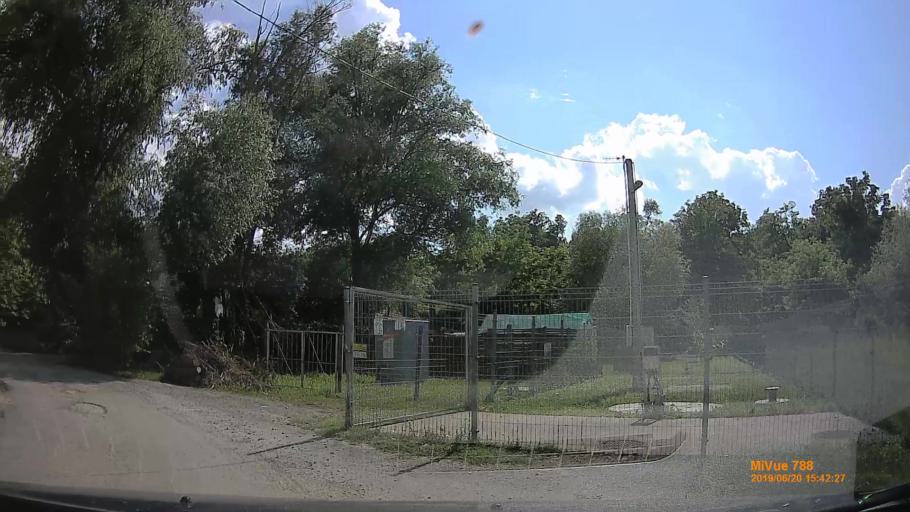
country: HU
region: Baranya
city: Kozarmisleny
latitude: 45.9857
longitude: 18.2627
